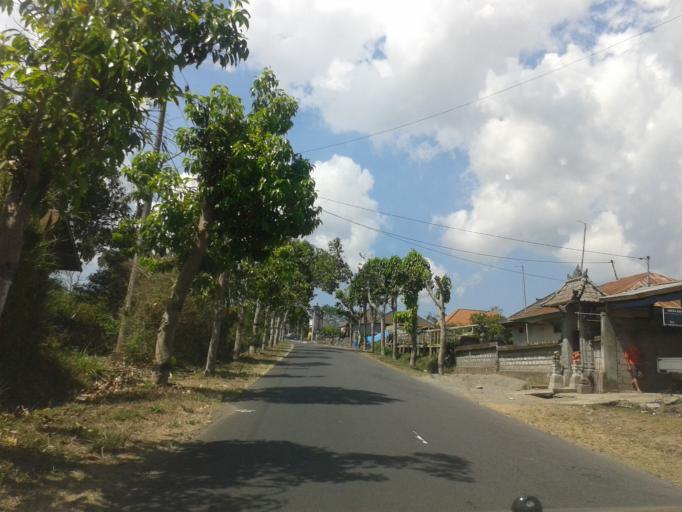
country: ID
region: Bali
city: Banjar Kedisan
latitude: -8.3066
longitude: 115.3356
